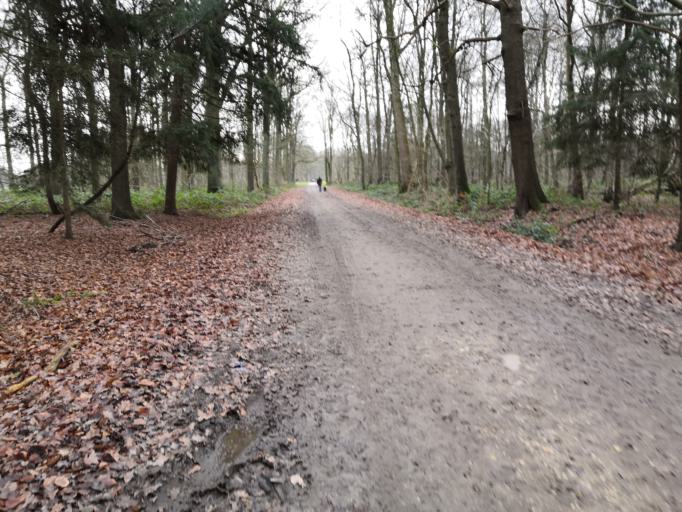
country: DE
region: North Rhine-Westphalia
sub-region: Regierungsbezirk Dusseldorf
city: Wachtendonk
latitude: 51.4389
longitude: 6.3642
